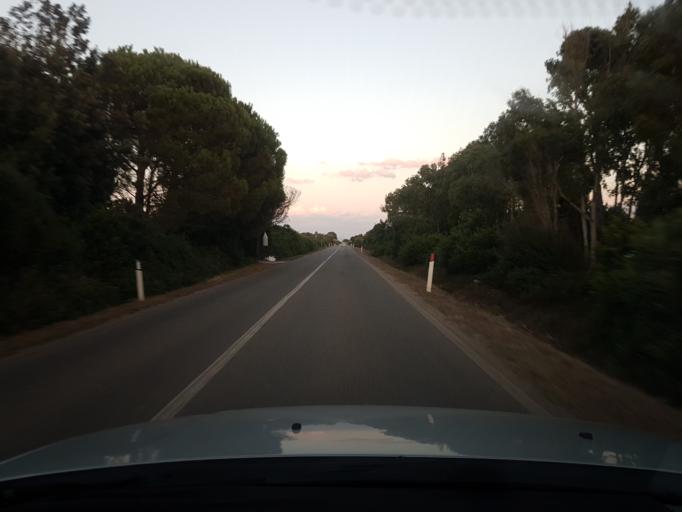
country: IT
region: Sardinia
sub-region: Provincia di Oristano
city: Riola Sardo
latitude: 40.0238
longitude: 8.4446
